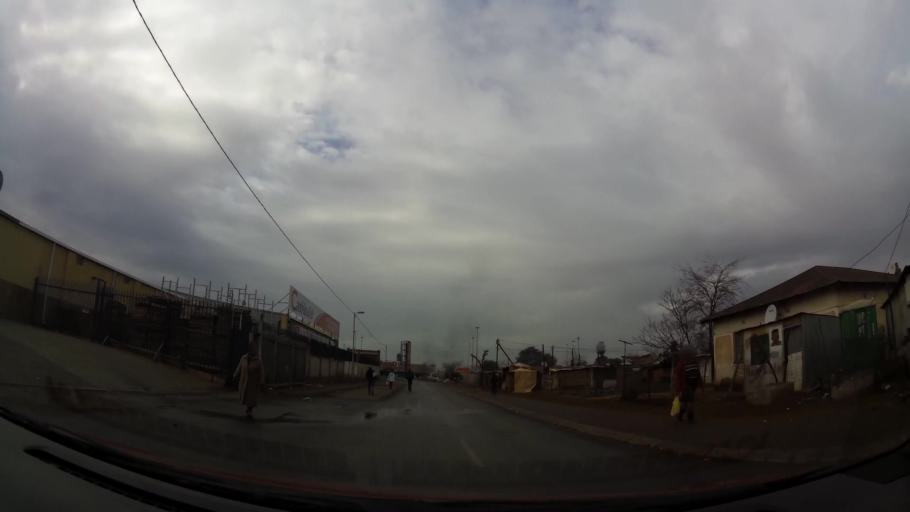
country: ZA
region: Gauteng
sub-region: City of Johannesburg Metropolitan Municipality
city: Soweto
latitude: -26.2874
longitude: 27.8469
